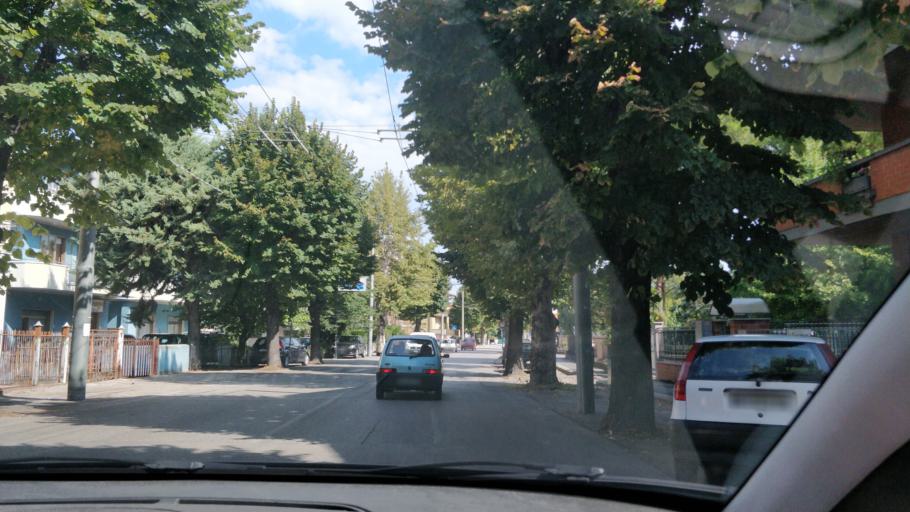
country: IT
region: Abruzzo
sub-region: Provincia di Chieti
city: Chieti
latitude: 42.3743
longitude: 14.1441
